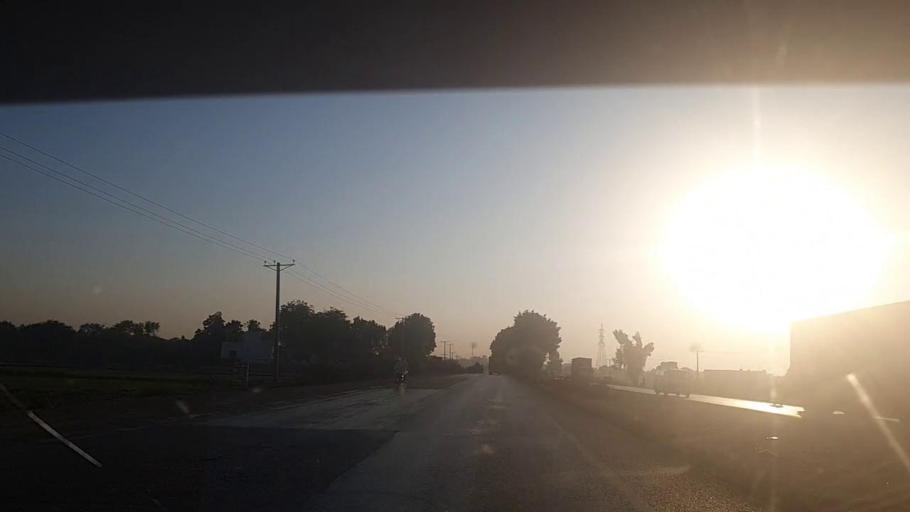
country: PK
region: Sindh
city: Hingorja
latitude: 27.1794
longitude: 68.3987
